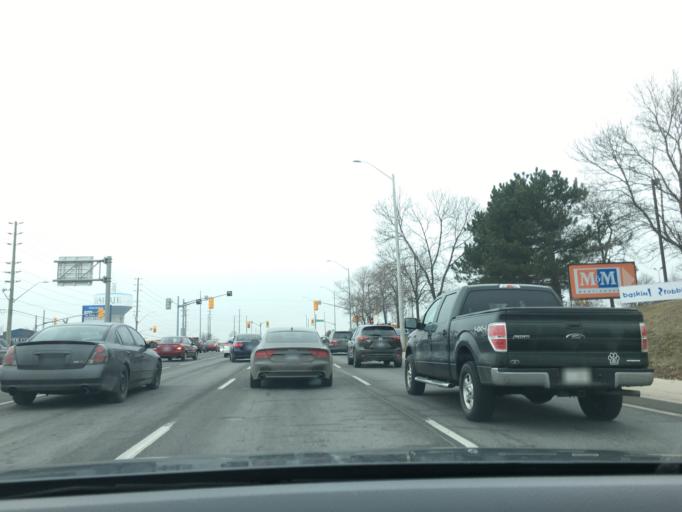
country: CA
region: Ontario
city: Innisfil
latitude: 44.3352
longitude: -79.6865
